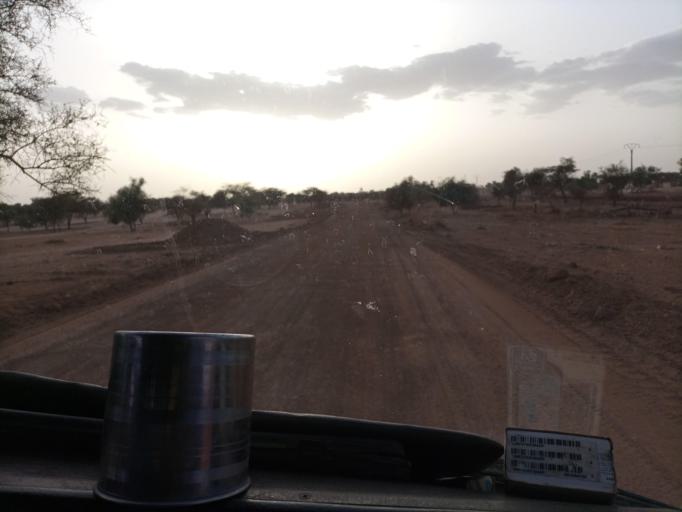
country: SN
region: Louga
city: Dara
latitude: 15.3720
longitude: -15.5823
